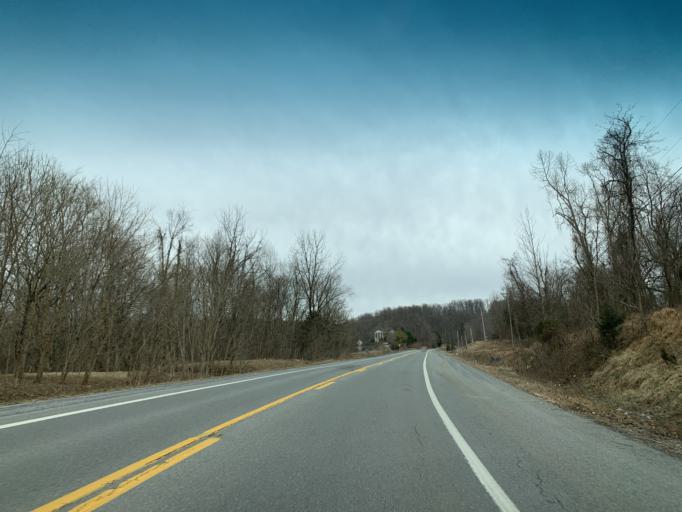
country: US
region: West Virginia
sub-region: Jefferson County
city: Shannondale
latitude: 39.2539
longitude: -77.8121
